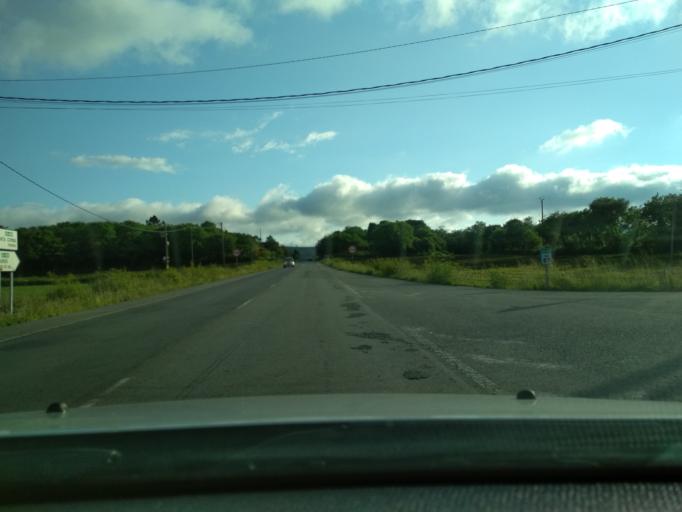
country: ES
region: Galicia
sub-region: Provincia da Coruna
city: Mazaricos
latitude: 42.9619
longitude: -8.9166
